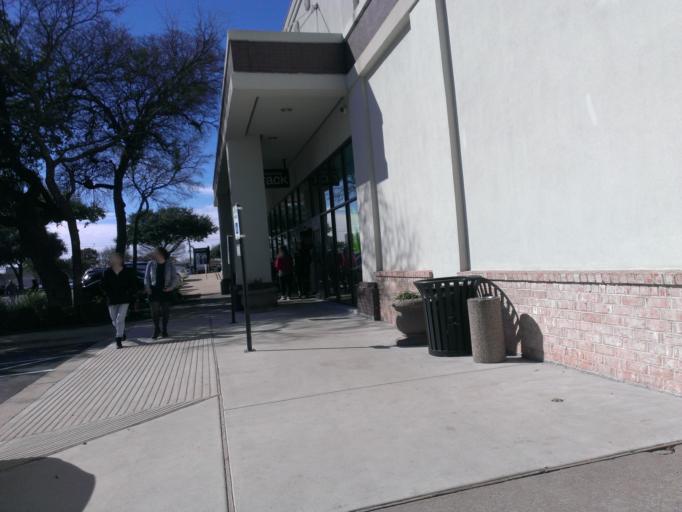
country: US
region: Texas
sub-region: Williamson County
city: Jollyville
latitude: 30.3893
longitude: -97.7420
